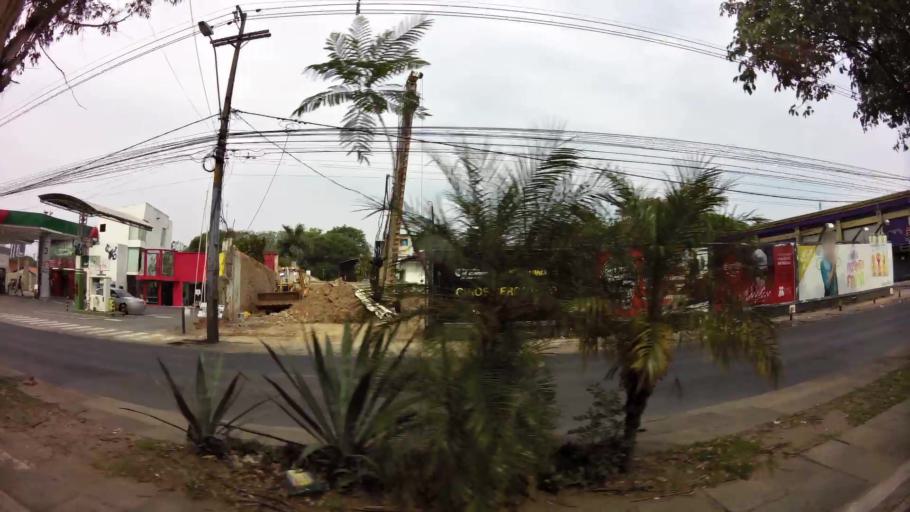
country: PY
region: Asuncion
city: Asuncion
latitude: -25.2883
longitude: -57.5729
